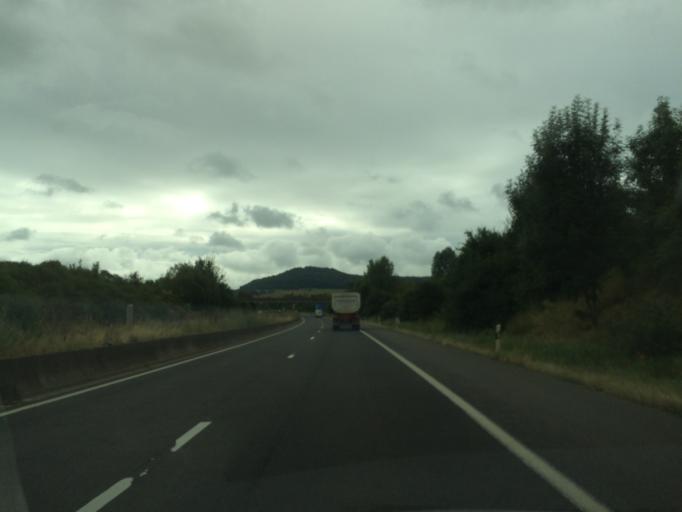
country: LU
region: Luxembourg
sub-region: Canton d'Esch-sur-Alzette
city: Kayl
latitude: 49.5055
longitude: 6.0396
